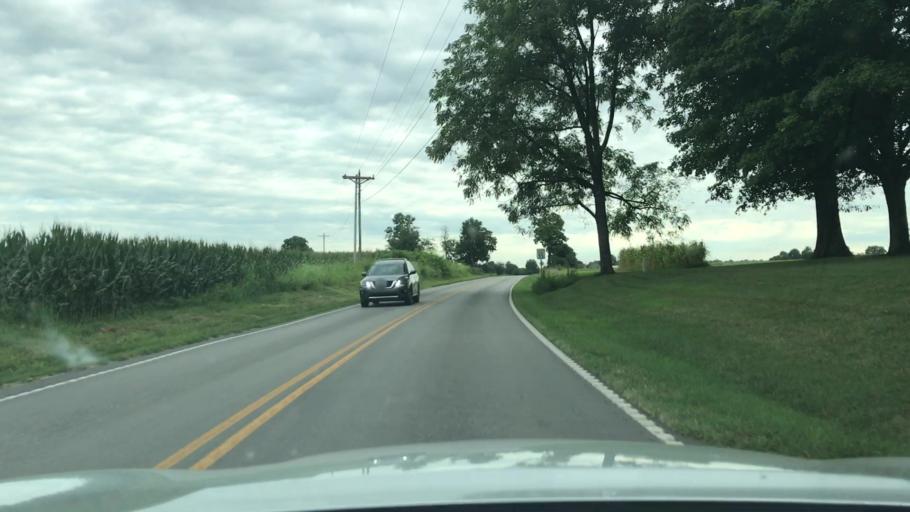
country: US
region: Kentucky
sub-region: Todd County
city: Guthrie
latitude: 36.7034
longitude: -87.1971
